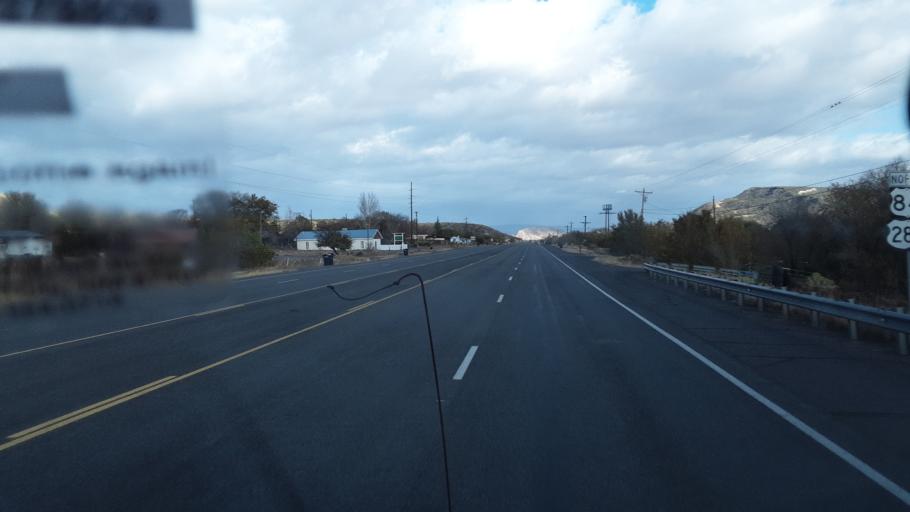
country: US
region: New Mexico
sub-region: Rio Arriba County
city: Ohkay Owingeh
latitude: 36.0574
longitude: -106.1170
